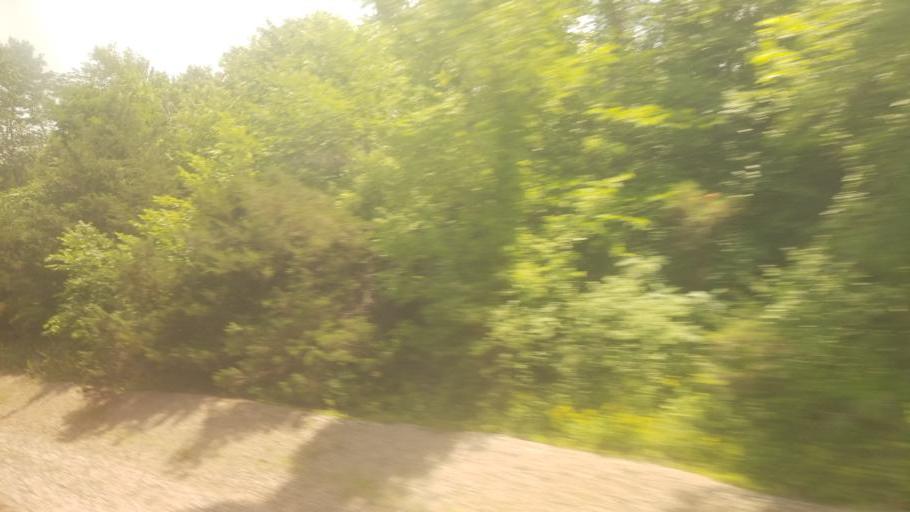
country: US
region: Missouri
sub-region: Macon County
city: La Plata
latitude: 40.0718
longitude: -92.4467
